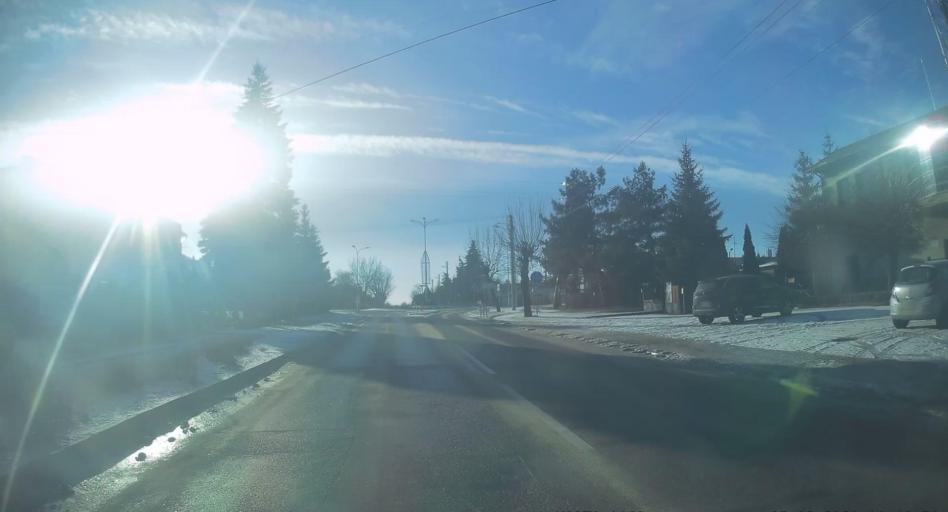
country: PL
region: Lodz Voivodeship
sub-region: Powiat rawski
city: Rawa Mazowiecka
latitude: 51.7526
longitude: 20.2415
